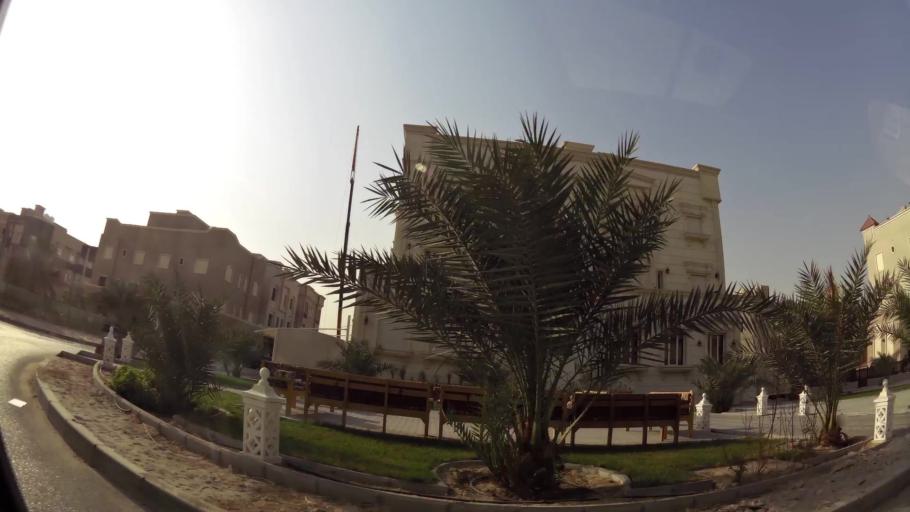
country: KW
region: Al Asimah
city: Ar Rabiyah
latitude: 29.3263
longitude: 47.8041
